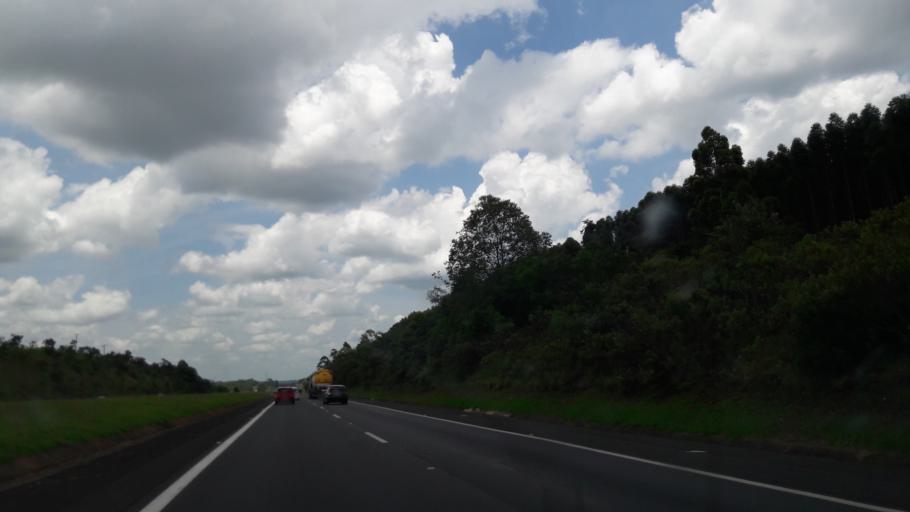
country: BR
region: Sao Paulo
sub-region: Itatinga
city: Itatinga
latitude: -23.0670
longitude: -48.5512
